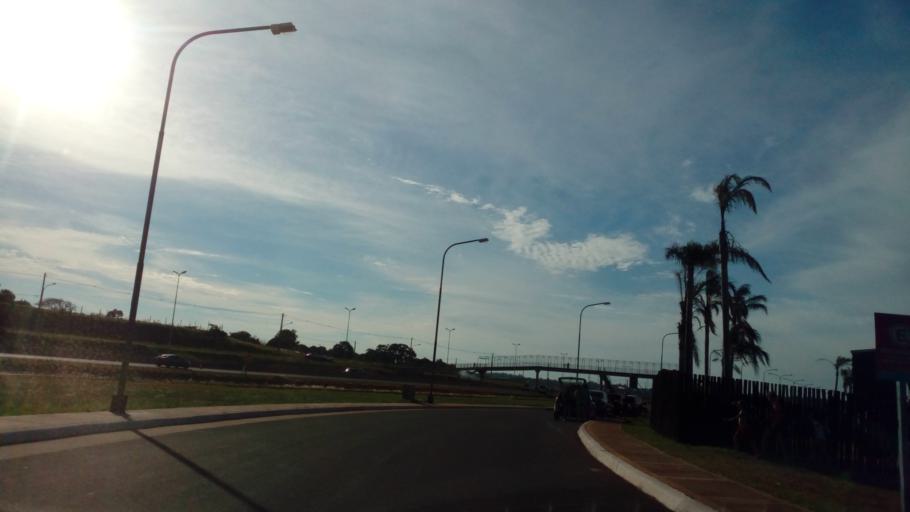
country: AR
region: Misiones
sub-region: Departamento de Capital
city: Posadas
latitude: -27.4207
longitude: -55.8775
